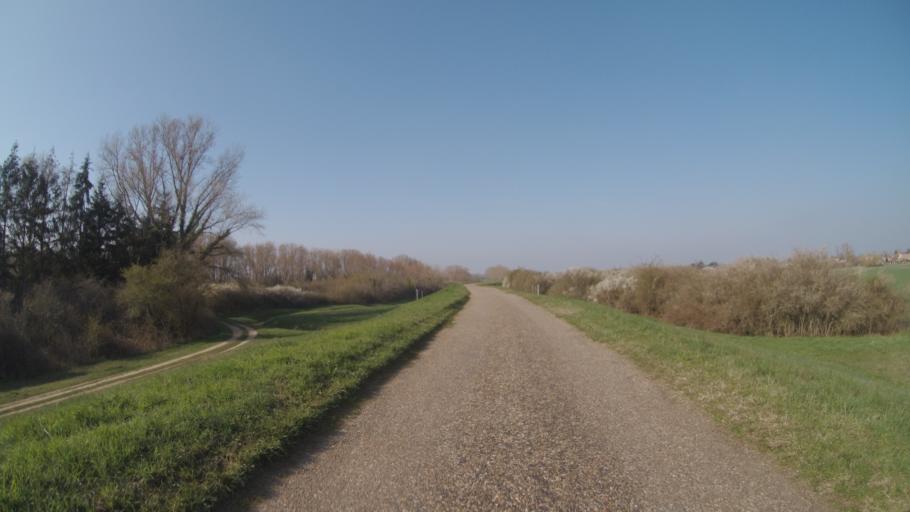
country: FR
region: Centre
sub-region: Departement du Loiret
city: Sandillon
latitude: 47.8699
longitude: 2.0368
